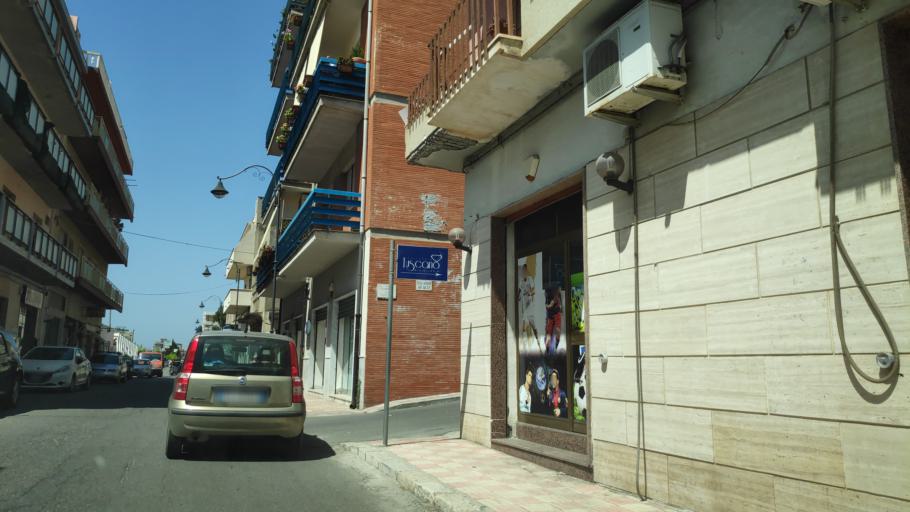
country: IT
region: Calabria
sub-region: Provincia di Reggio Calabria
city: Bova Marina
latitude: 37.9307
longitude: 15.9231
